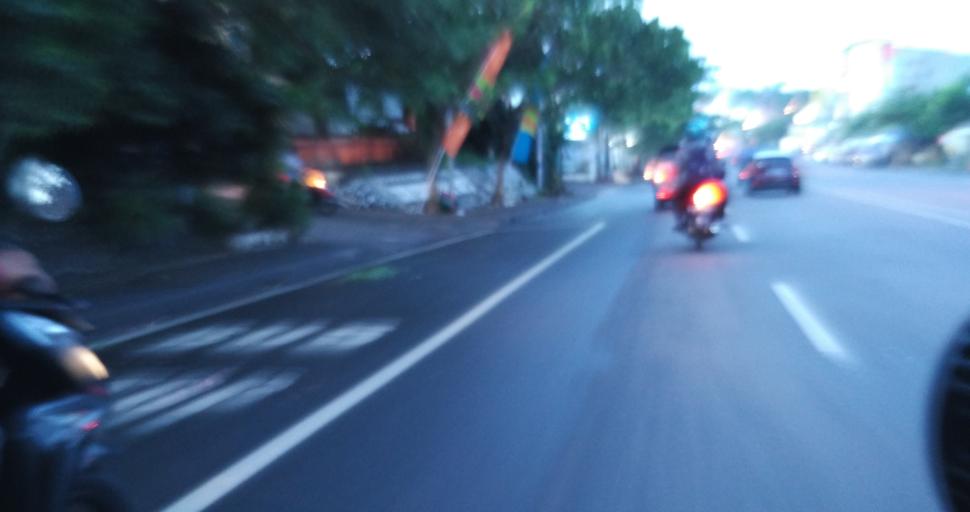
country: ID
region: Central Java
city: Semarang
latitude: -7.0516
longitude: 110.4175
